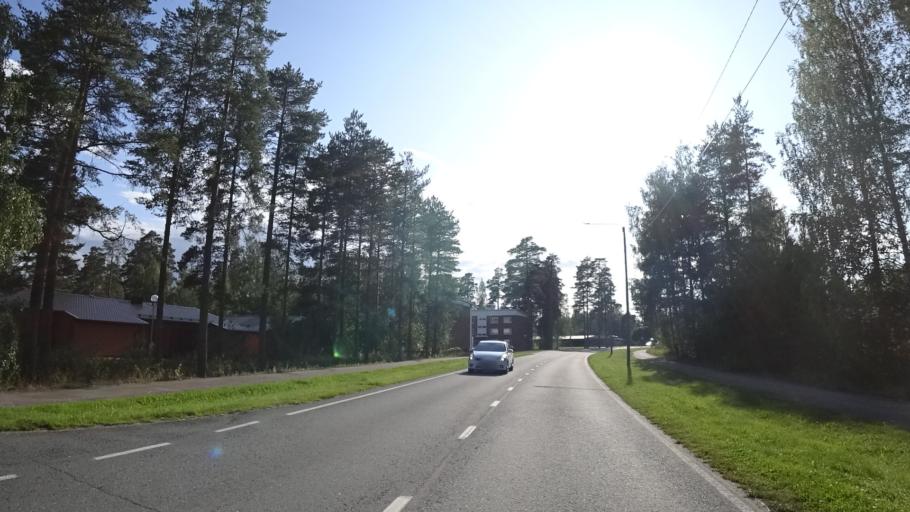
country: FI
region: North Karelia
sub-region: Keski-Karjala
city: Kesaelahti
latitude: 61.8917
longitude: 29.8405
